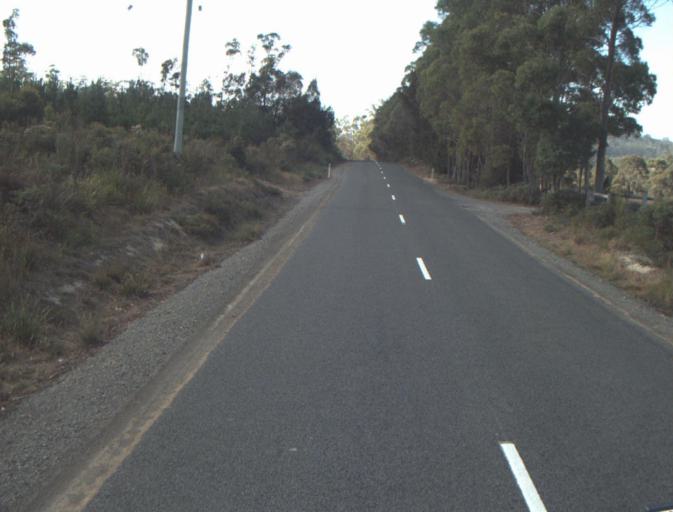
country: AU
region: Tasmania
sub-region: Dorset
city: Bridport
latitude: -41.1426
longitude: 147.2287
